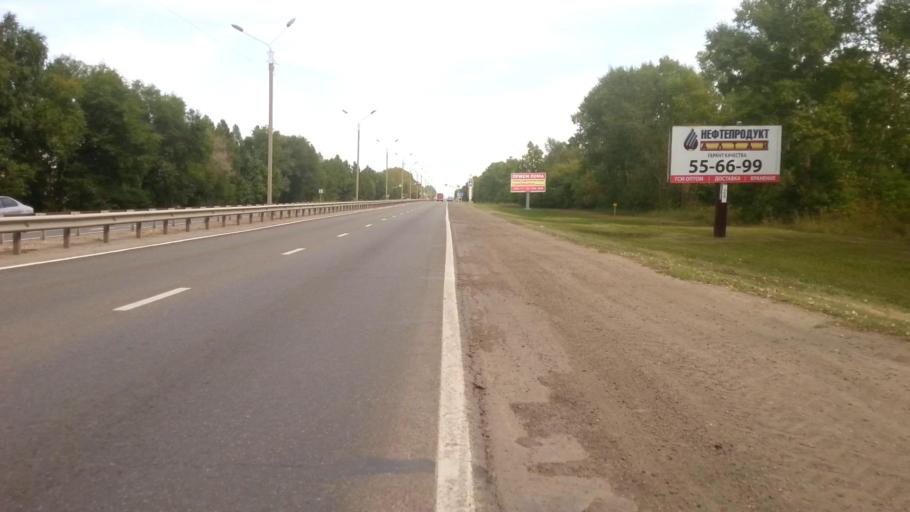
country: RU
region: Altai Krai
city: Vlasikha
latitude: 53.3530
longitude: 83.5626
